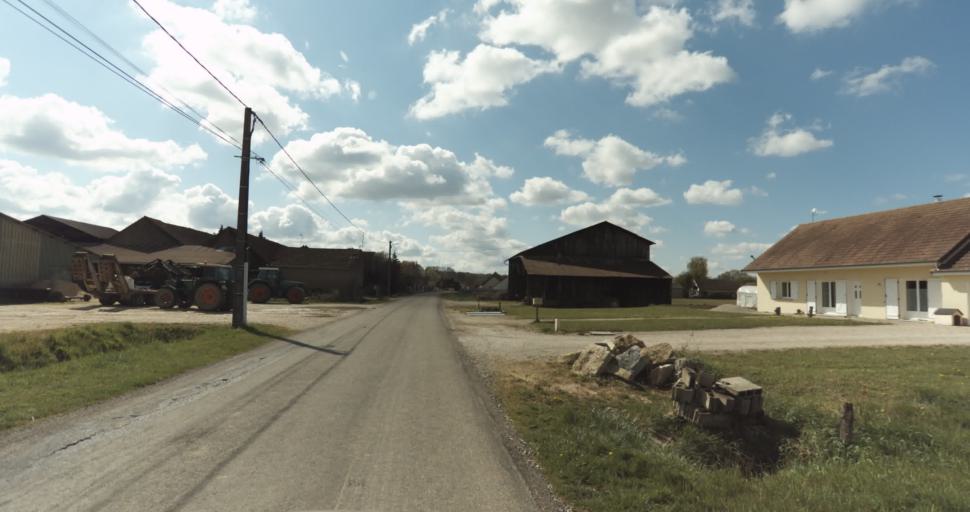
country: FR
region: Bourgogne
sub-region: Departement de la Cote-d'Or
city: Auxonne
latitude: 47.2010
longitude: 5.4256
